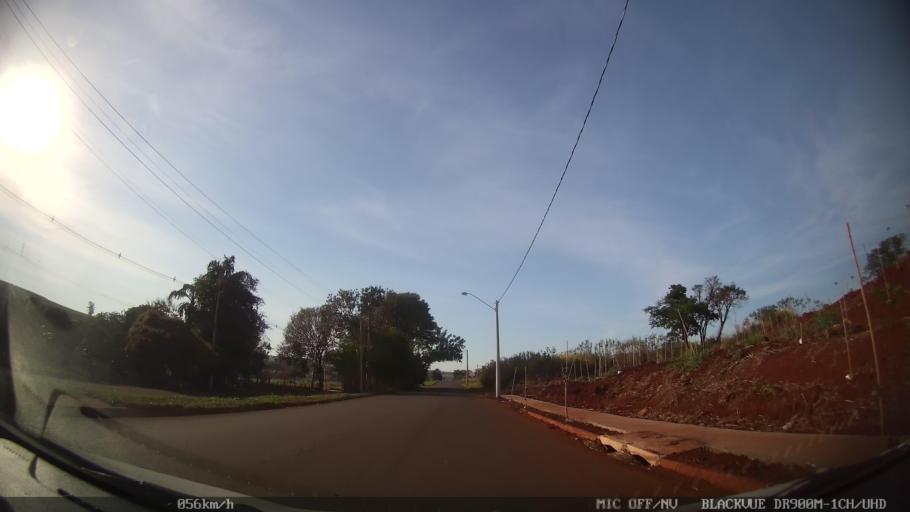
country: BR
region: Sao Paulo
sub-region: Ribeirao Preto
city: Ribeirao Preto
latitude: -21.2749
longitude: -47.8097
